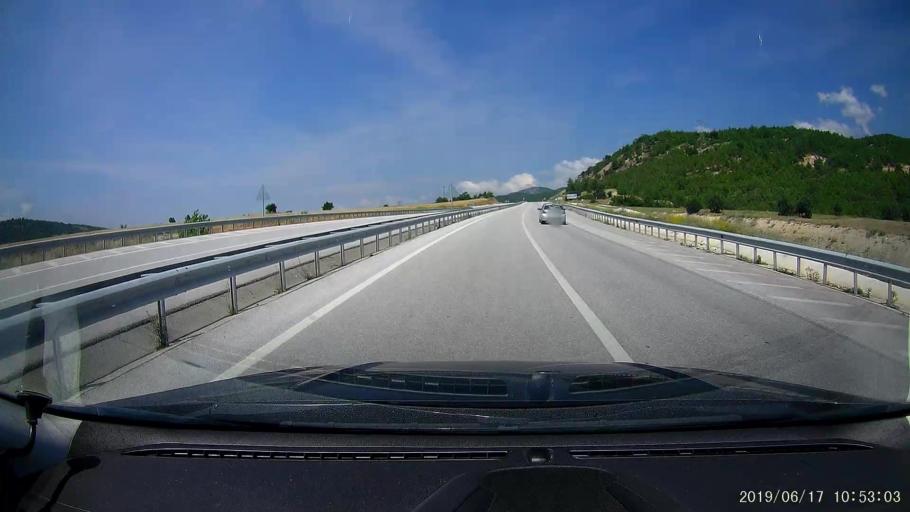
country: TR
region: Corum
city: Hacihamza
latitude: 41.0828
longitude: 34.3308
